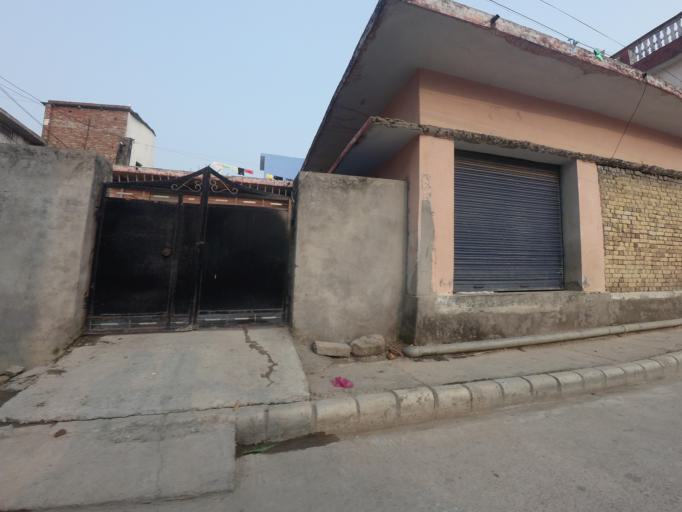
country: NP
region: Western Region
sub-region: Lumbini Zone
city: Bhairahawa
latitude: 27.5167
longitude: 83.4461
